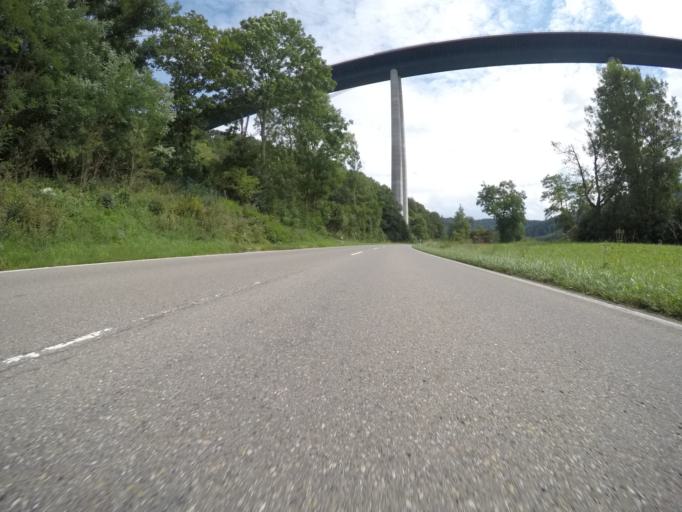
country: DE
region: Baden-Wuerttemberg
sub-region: Karlsruhe Region
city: Horb am Neckar
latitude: 48.4509
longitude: 8.7655
